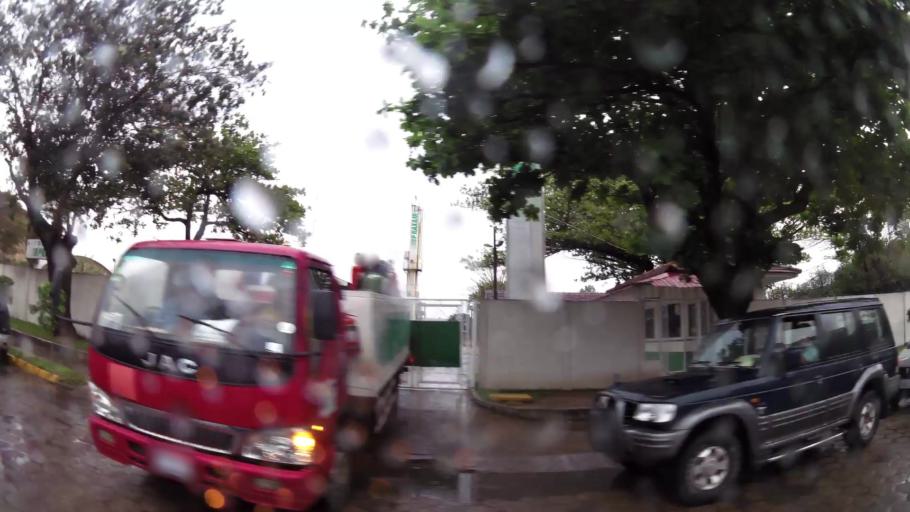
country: BO
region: Santa Cruz
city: Santa Cruz de la Sierra
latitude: -17.7653
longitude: -63.1427
